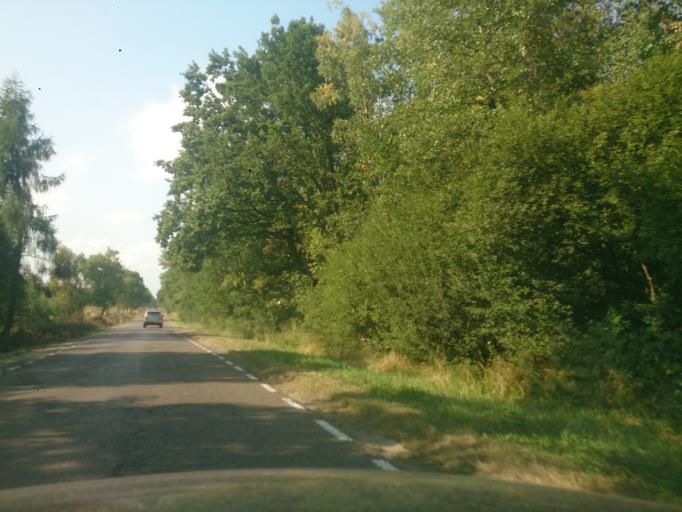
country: PL
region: Swietokrzyskie
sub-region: Powiat opatowski
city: Iwaniska
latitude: 50.7009
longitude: 21.3315
